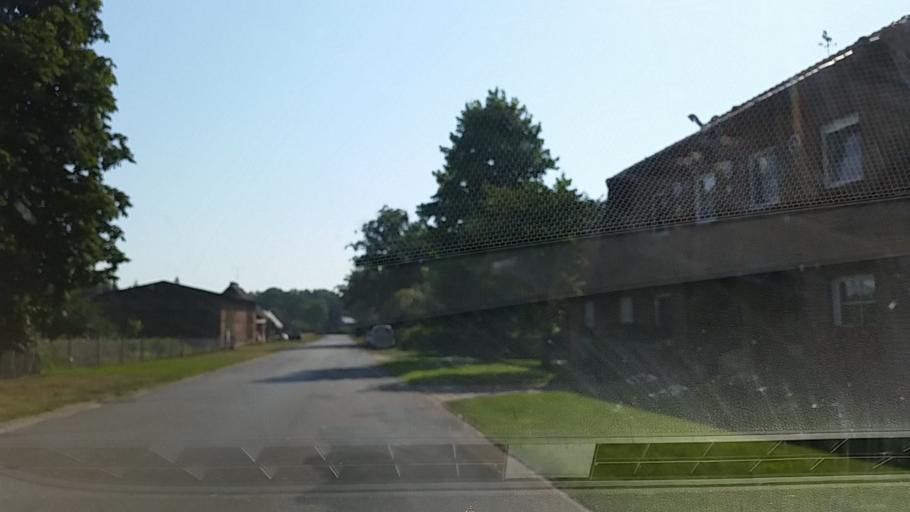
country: DE
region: Lower Saxony
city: Luder
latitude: 52.8088
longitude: 10.6298
